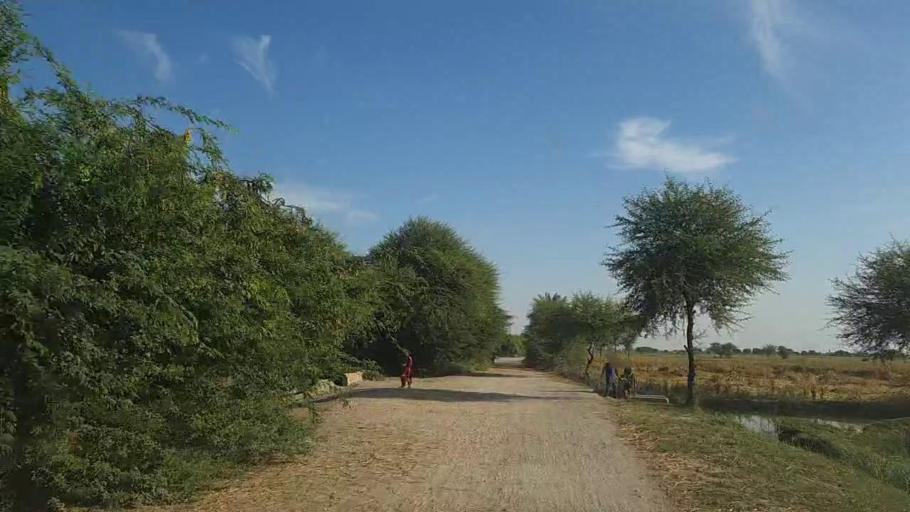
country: PK
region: Sindh
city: Mirpur Batoro
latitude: 24.7660
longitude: 68.3485
